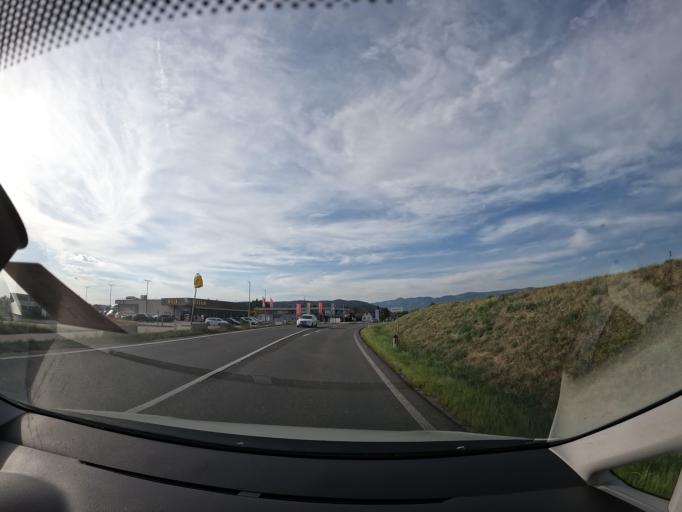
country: AT
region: Carinthia
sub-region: Politischer Bezirk Volkermarkt
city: Voelkermarkt
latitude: 46.6284
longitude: 14.6345
